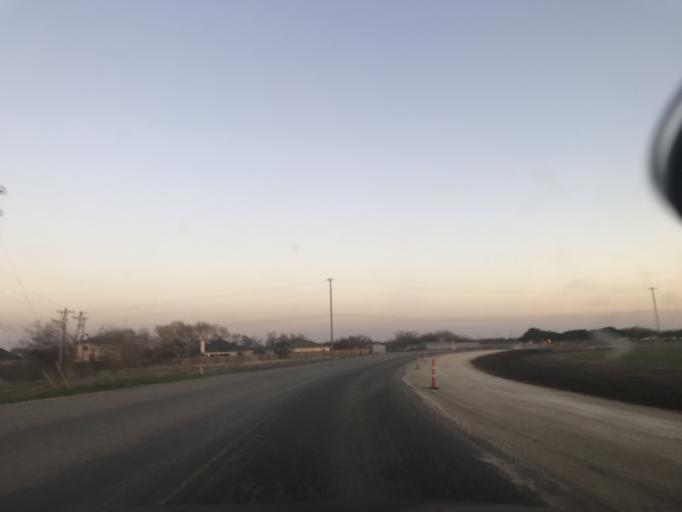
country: US
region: Texas
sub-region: Williamson County
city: Hutto
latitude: 30.5181
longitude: -97.5379
